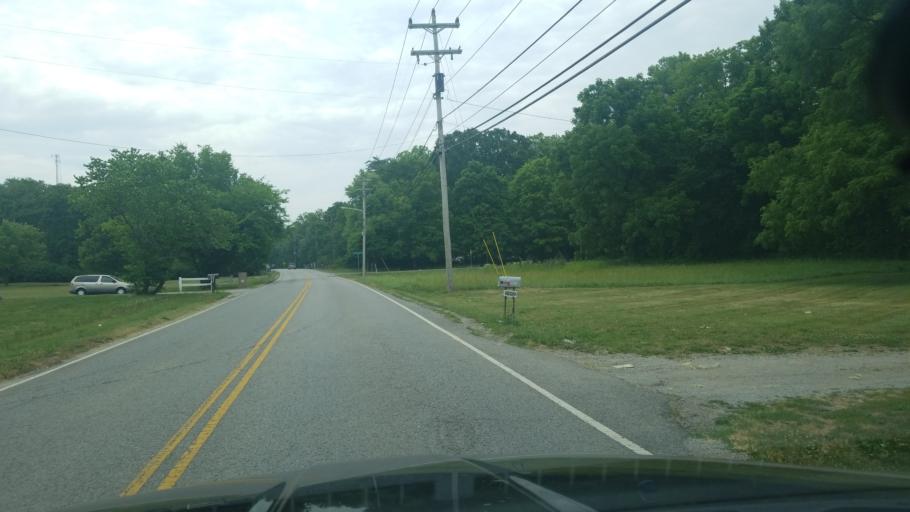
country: US
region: Tennessee
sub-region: Davidson County
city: Goodlettsville
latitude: 36.2552
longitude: -86.7515
